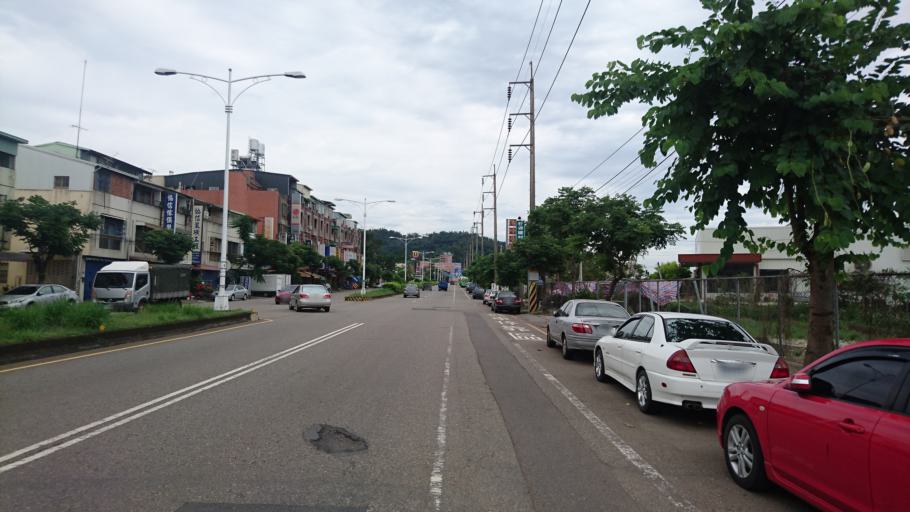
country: TW
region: Taiwan
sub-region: Taichung City
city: Taichung
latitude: 24.0585
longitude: 120.6953
